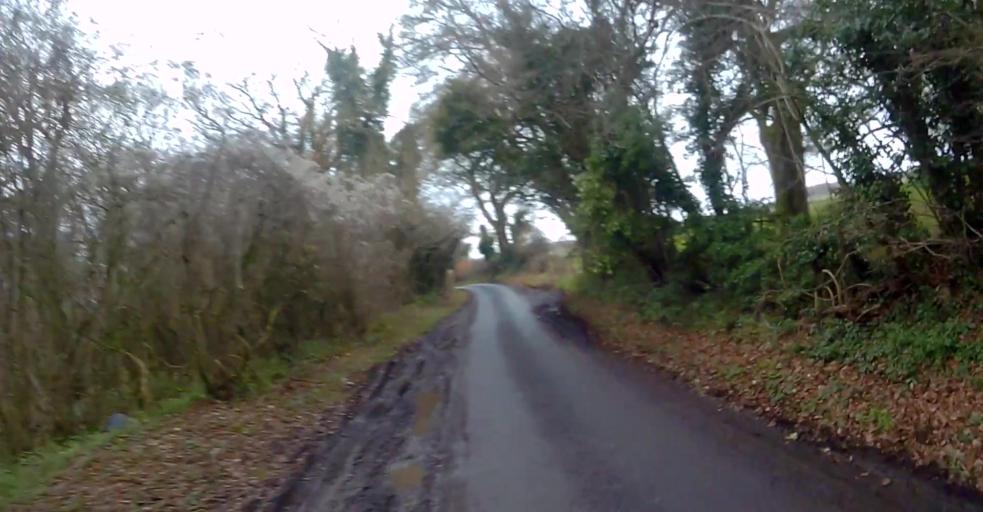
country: GB
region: England
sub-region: Hampshire
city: Overton
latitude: 51.2211
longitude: -1.2258
